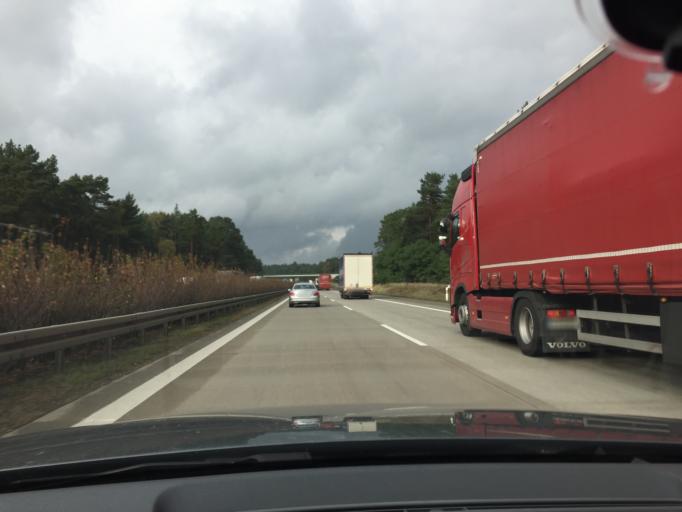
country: DE
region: Brandenburg
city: Schwerin
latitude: 52.1919
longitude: 13.6157
